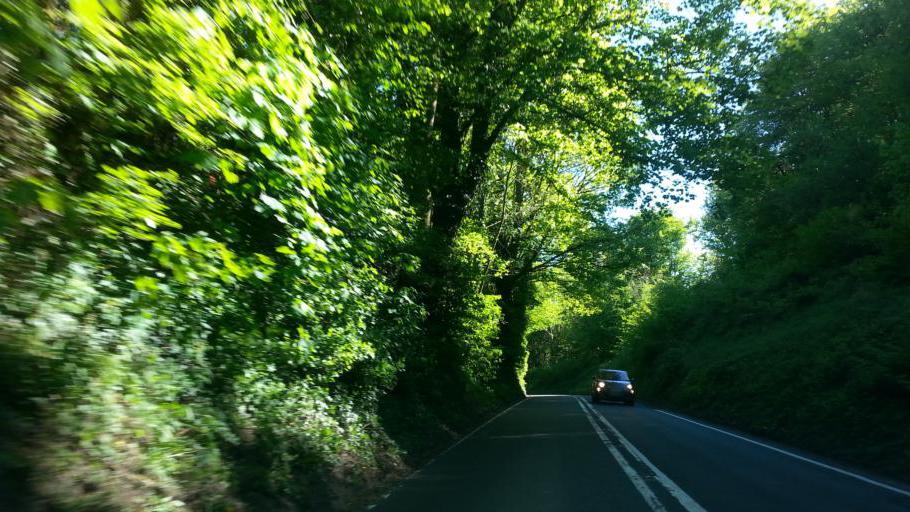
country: GB
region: England
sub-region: Dorset
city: Shaftesbury
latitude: 51.0279
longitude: -2.1902
